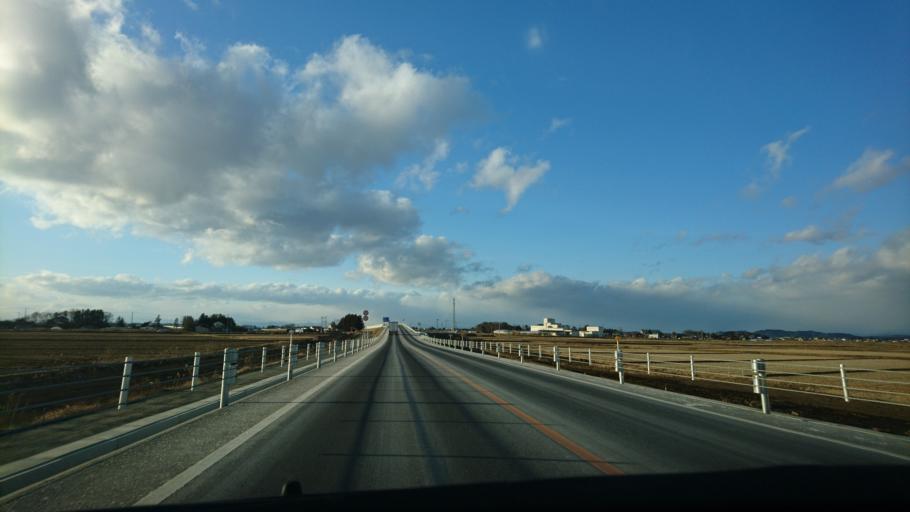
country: JP
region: Miyagi
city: Wakuya
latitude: 38.6810
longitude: 141.2547
